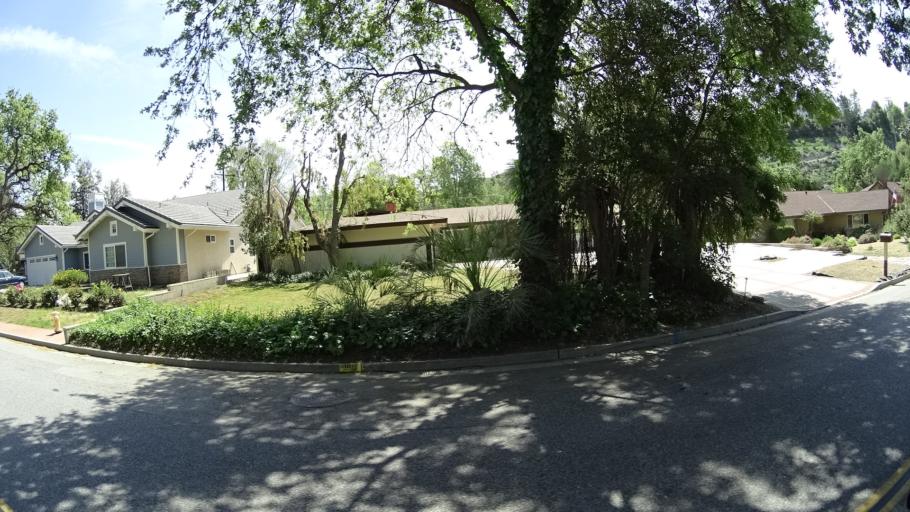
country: US
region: California
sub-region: Ventura County
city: Thousand Oaks
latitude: 34.2028
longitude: -118.8495
